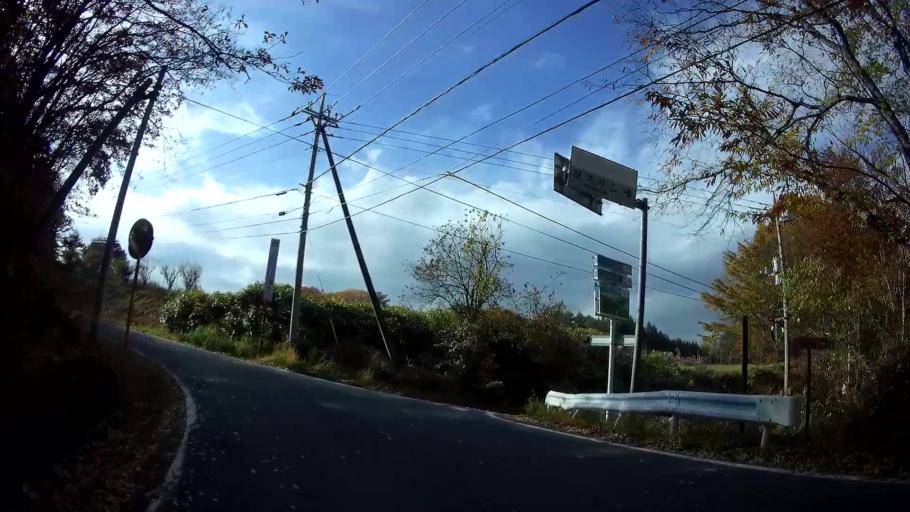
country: JP
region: Gunma
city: Nakanojomachi
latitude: 36.6219
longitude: 138.6320
